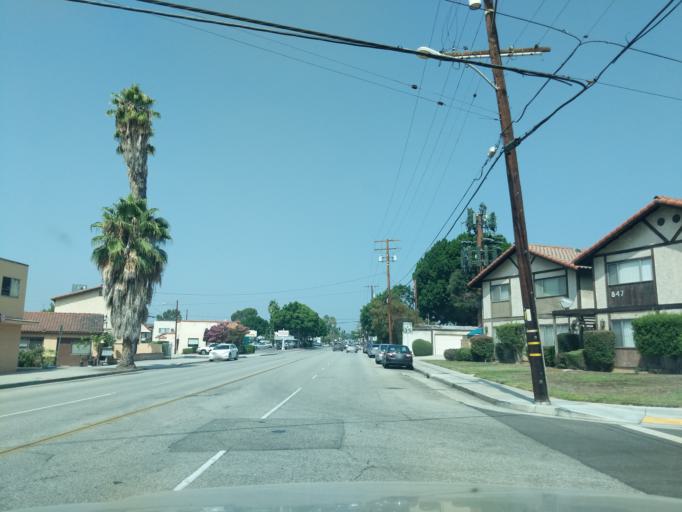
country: US
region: California
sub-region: Los Angeles County
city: East San Gabriel
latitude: 34.0901
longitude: -118.0884
